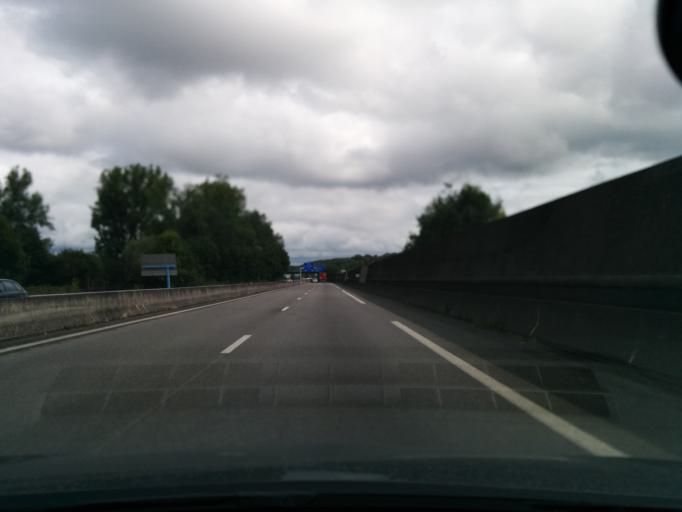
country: FR
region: Limousin
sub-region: Departement de la Correze
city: Ussac
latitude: 45.1723
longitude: 1.4867
